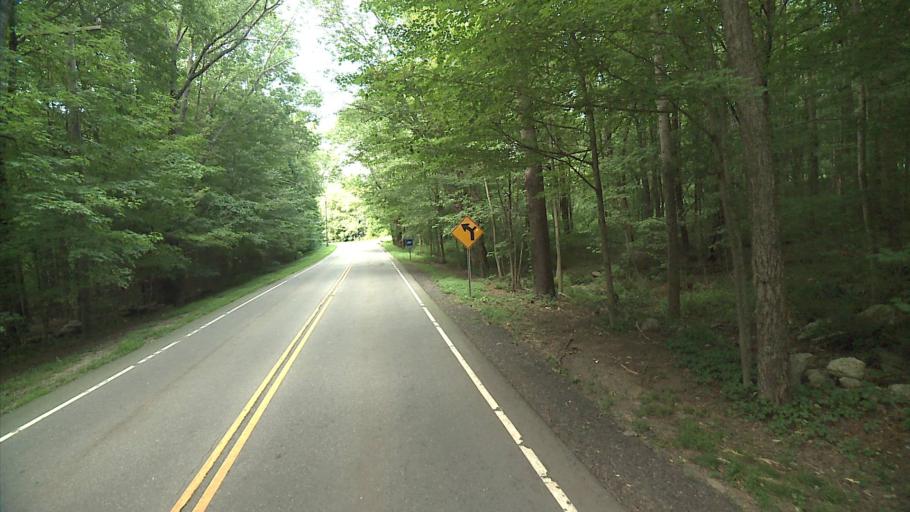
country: US
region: Connecticut
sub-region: New London County
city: Colchester
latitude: 41.6289
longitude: -72.2915
